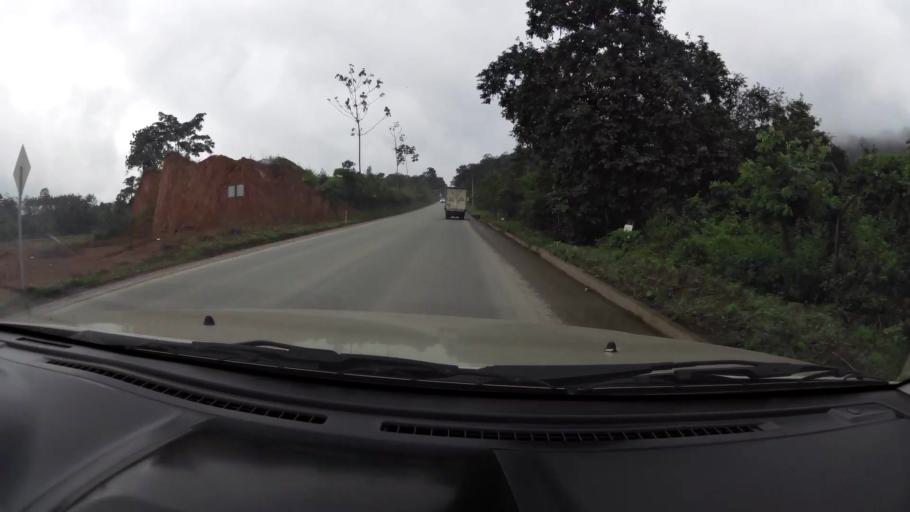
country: EC
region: El Oro
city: Pasaje
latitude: -3.3290
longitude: -79.7653
